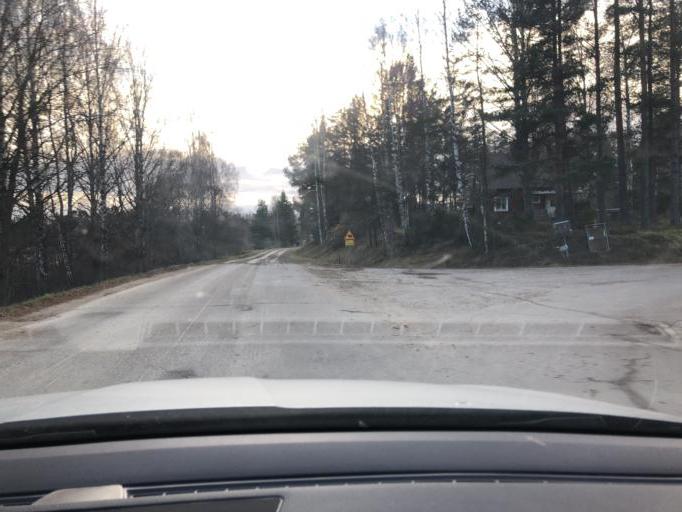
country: SE
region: Gaevleborg
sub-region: Hudiksvalls Kommun
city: Sorforsa
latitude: 61.7354
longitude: 16.9259
